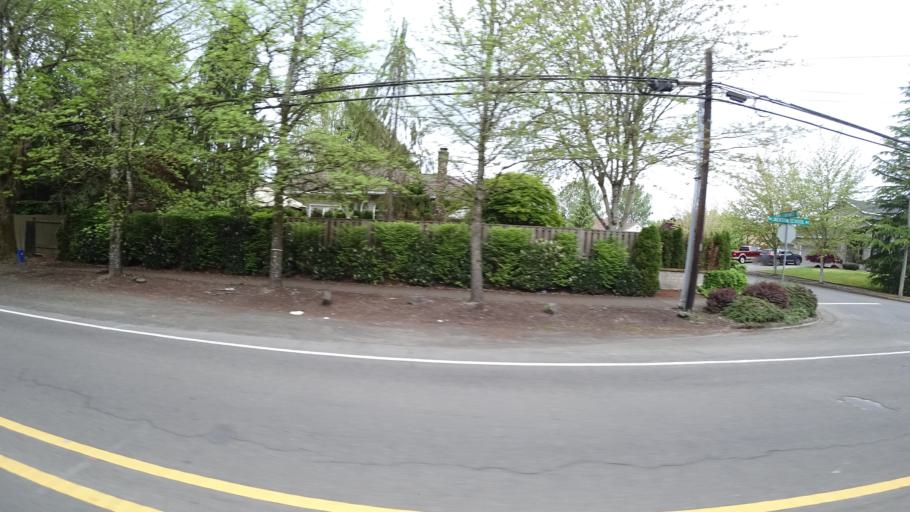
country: US
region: Oregon
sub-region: Washington County
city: Hillsboro
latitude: 45.5487
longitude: -122.9797
